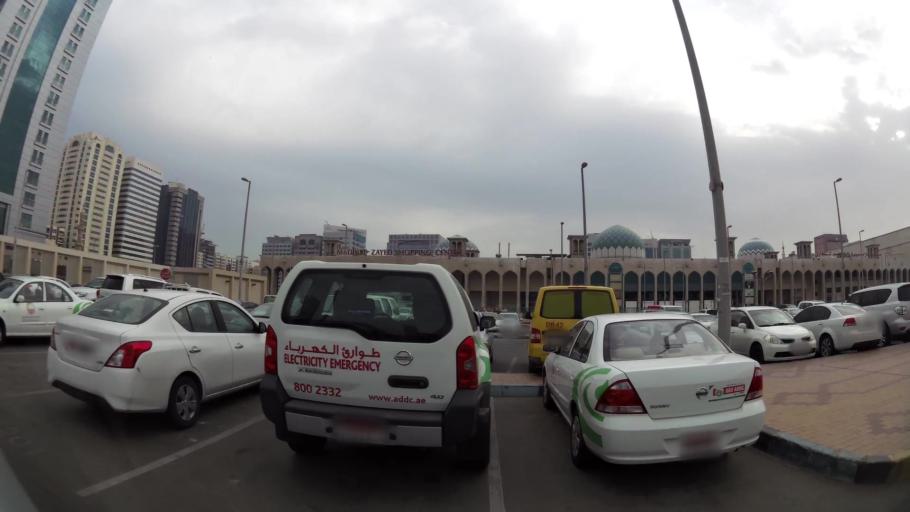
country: AE
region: Abu Dhabi
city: Abu Dhabi
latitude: 24.4835
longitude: 54.3639
